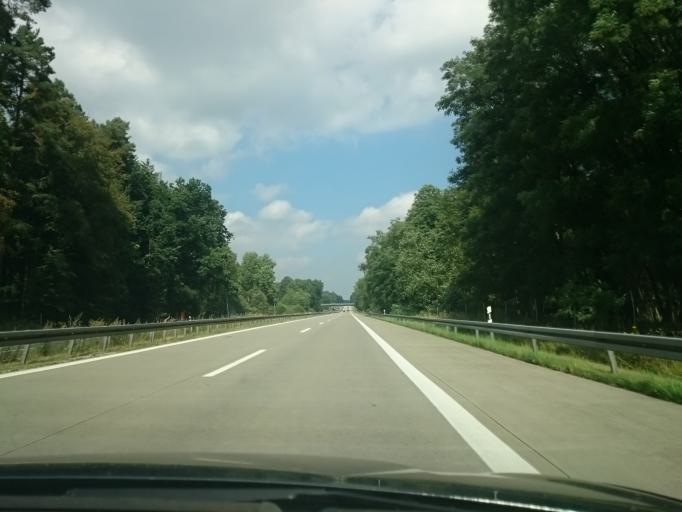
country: DE
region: Brandenburg
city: Althuttendorf
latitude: 53.0325
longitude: 13.8313
